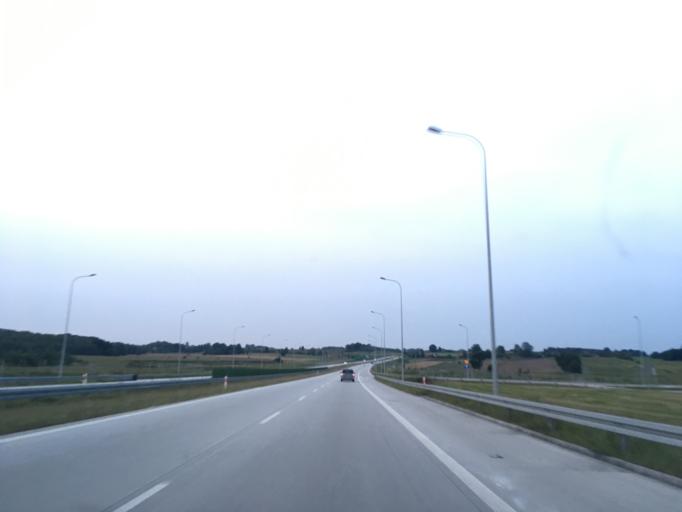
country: PL
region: Lodz Voivodeship
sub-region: Powiat zgierski
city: Strykow
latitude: 51.8418
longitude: 19.6589
